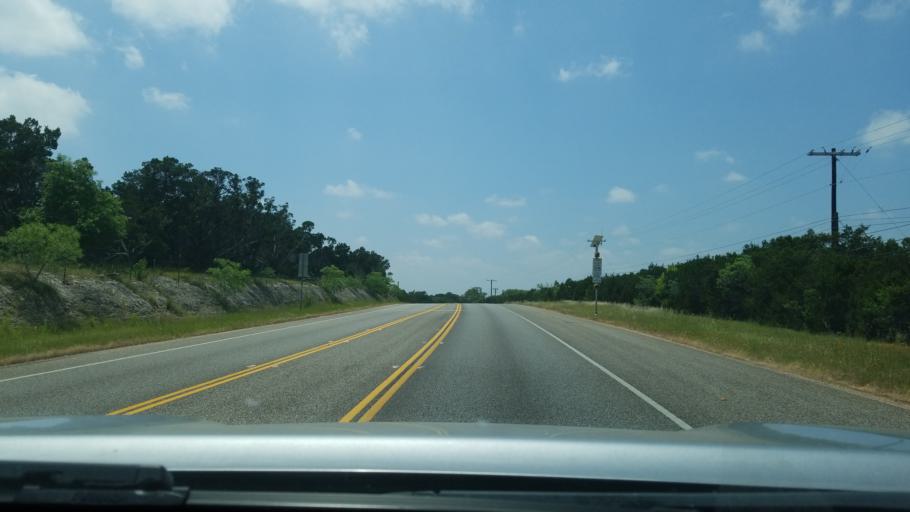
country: US
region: Texas
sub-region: Hays County
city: Woodcreek
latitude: 30.0192
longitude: -98.1400
